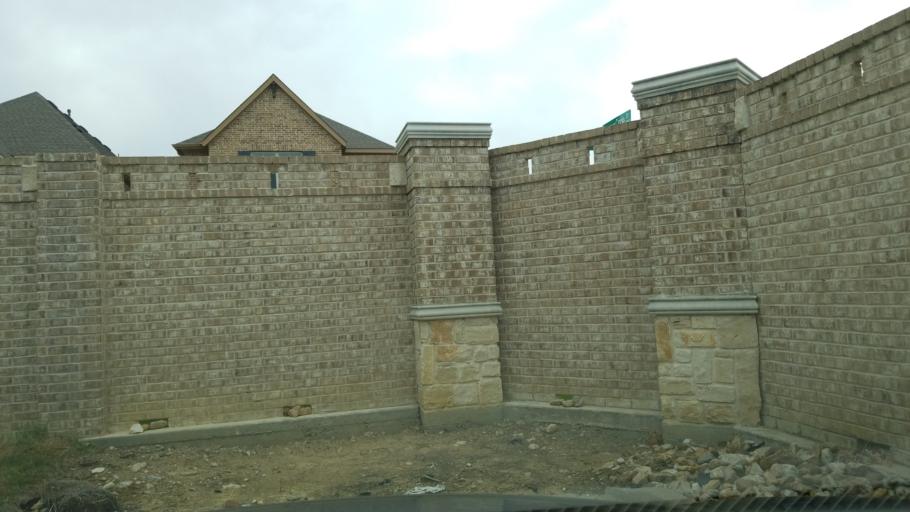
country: US
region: Texas
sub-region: Dallas County
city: Coppell
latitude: 32.8996
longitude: -96.9853
